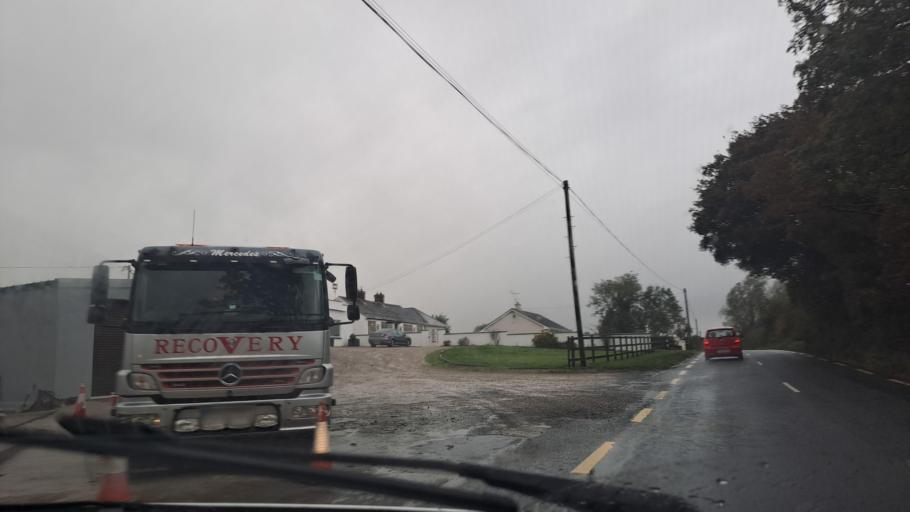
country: GB
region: Northern Ireland
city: Crossmaglen
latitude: 53.9711
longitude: -6.5926
